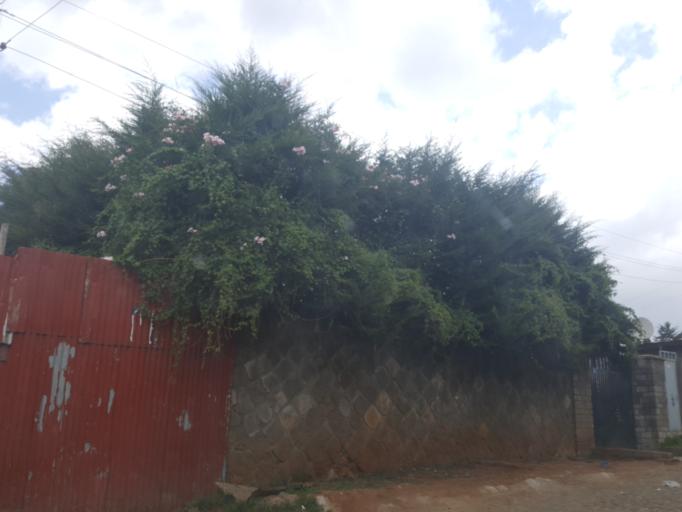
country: ET
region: Adis Abeba
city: Addis Ababa
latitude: 9.0628
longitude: 38.7180
